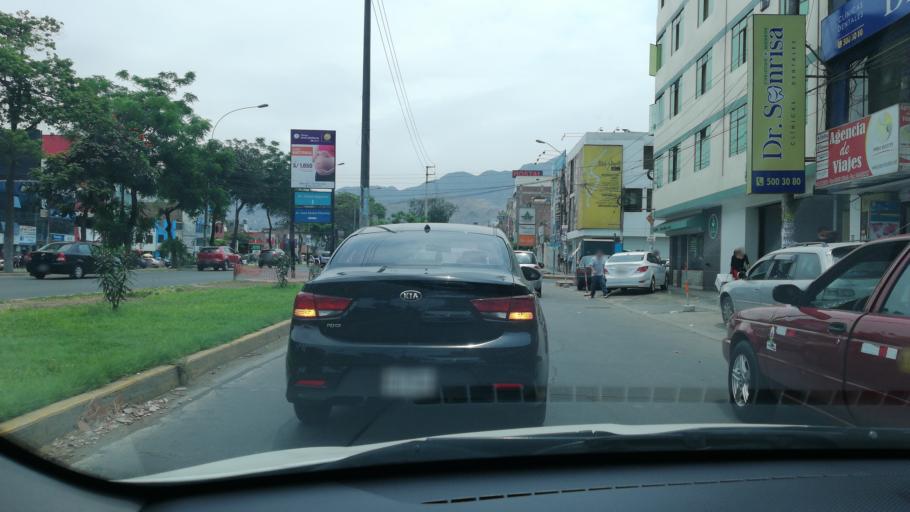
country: PE
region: Lima
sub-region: Lima
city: Independencia
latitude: -11.9909
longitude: -77.0685
